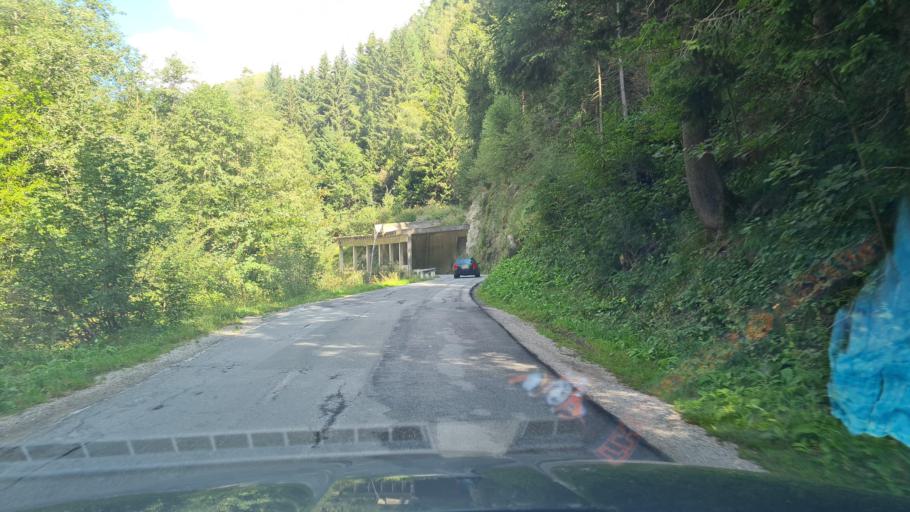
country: AT
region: Salzburg
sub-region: Politischer Bezirk Tamsweg
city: Zederhaus
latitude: 47.1771
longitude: 13.4464
